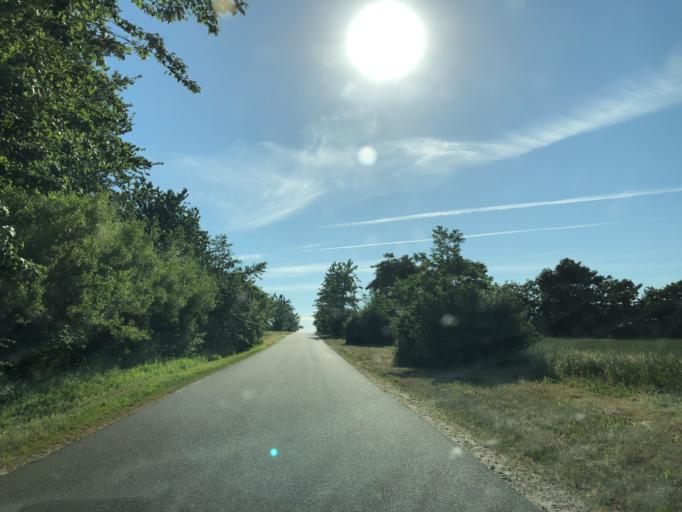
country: DK
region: Central Jutland
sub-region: Holstebro Kommune
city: Ulfborg
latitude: 56.3236
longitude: 8.3648
